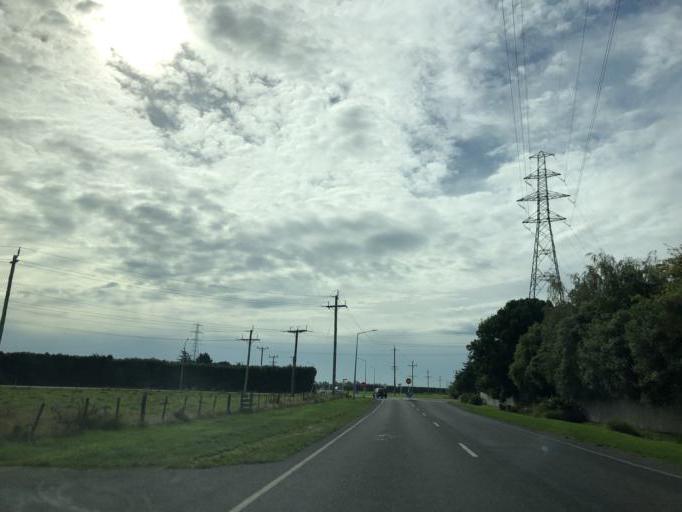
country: NZ
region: Canterbury
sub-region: Selwyn District
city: Lincoln
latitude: -43.6370
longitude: 172.4503
